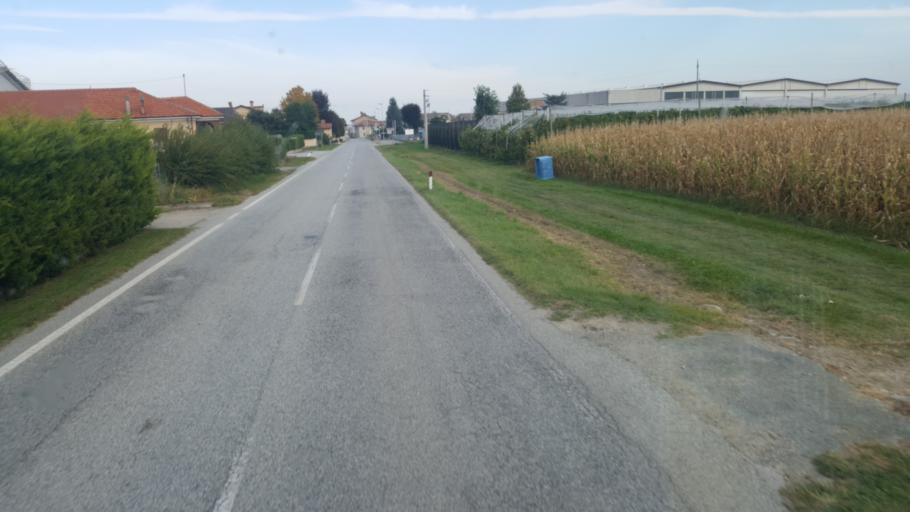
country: IT
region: Piedmont
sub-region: Provincia di Cuneo
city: Verzuolo
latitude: 44.5976
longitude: 7.5056
